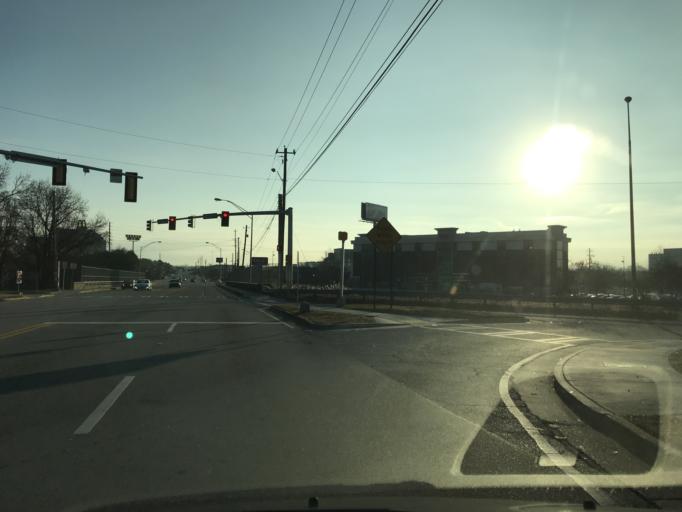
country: US
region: Georgia
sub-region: Fulton County
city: College Park
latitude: 33.6591
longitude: -84.4326
